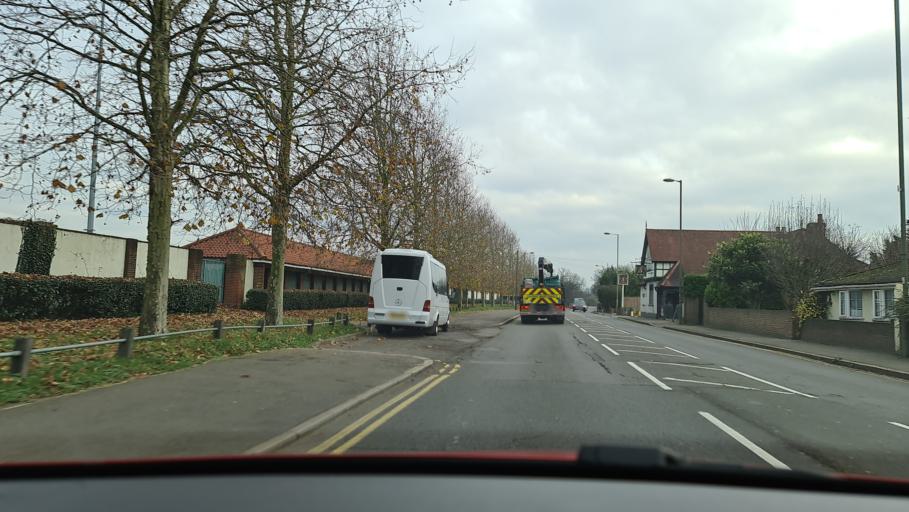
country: GB
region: England
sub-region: Surrey
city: Sunbury-on-Thames
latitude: 51.4171
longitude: -0.4065
